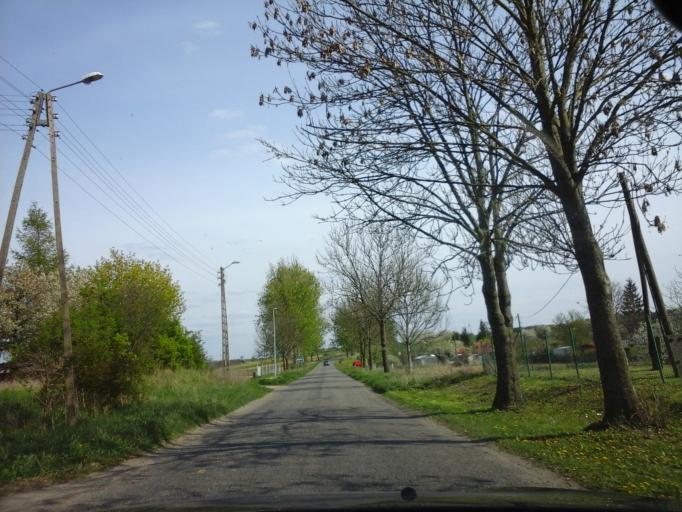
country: PL
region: West Pomeranian Voivodeship
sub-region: Powiat choszczenski
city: Krzecin
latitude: 53.0776
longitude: 15.4928
